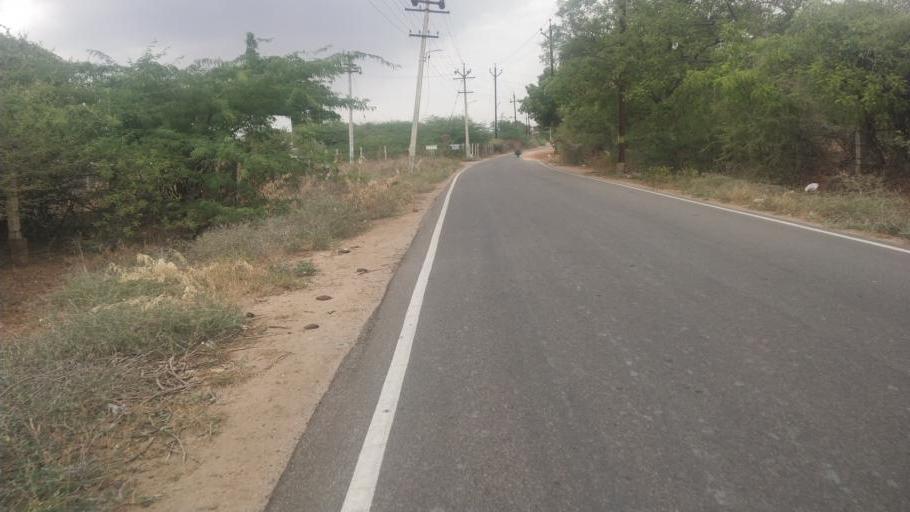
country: IN
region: Tamil Nadu
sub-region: Tirunelveli Kattabo
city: Tirunelveli
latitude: 8.6895
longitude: 77.7238
